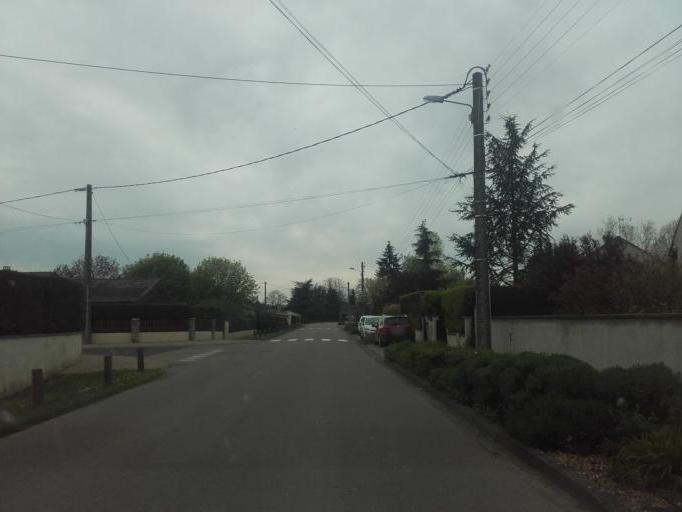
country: FR
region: Bourgogne
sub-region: Departement de Saone-et-Loire
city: Demigny
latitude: 46.9508
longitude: 4.8448
